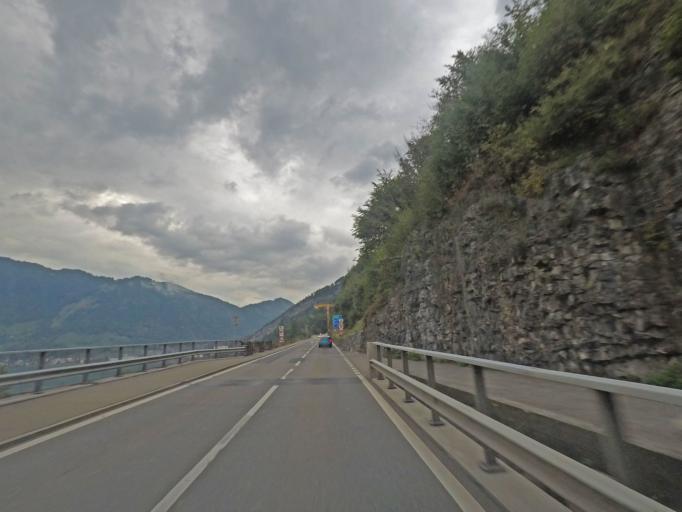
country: CH
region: Schwyz
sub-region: Bezirk Schwyz
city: Ingenbohl
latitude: 46.9792
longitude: 8.6118
